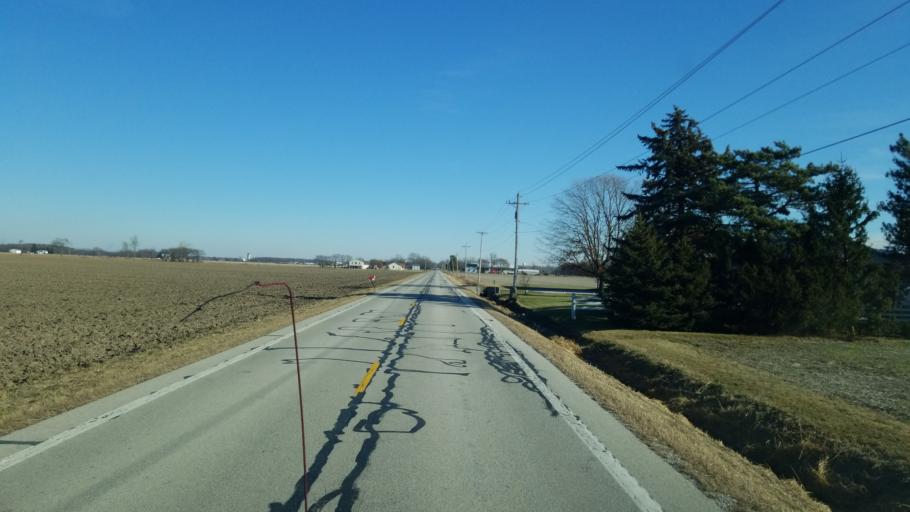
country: US
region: Ohio
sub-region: Wood County
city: Luckey
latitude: 41.4570
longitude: -83.5088
